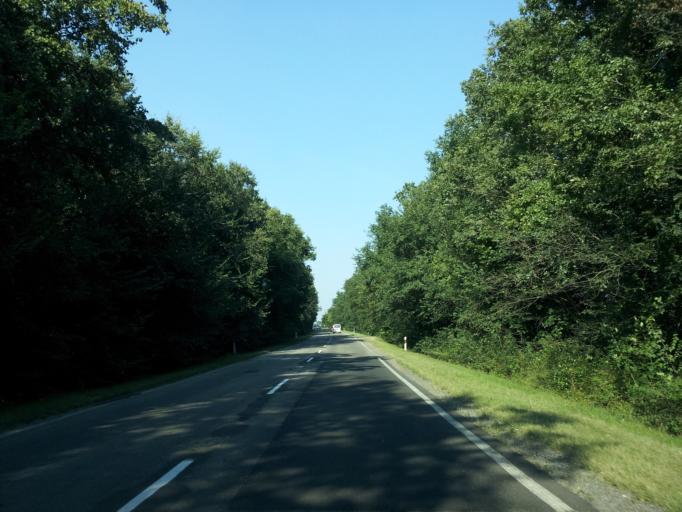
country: HU
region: Fejer
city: Polgardi
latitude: 47.0260
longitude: 18.2858
